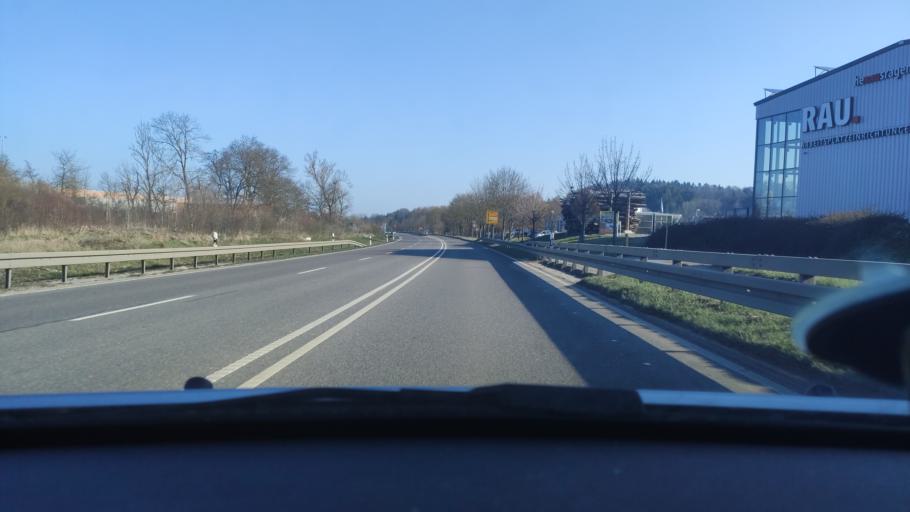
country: DE
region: Baden-Wuerttemberg
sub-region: Tuebingen Region
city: Balingen
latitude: 48.2523
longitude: 8.8552
